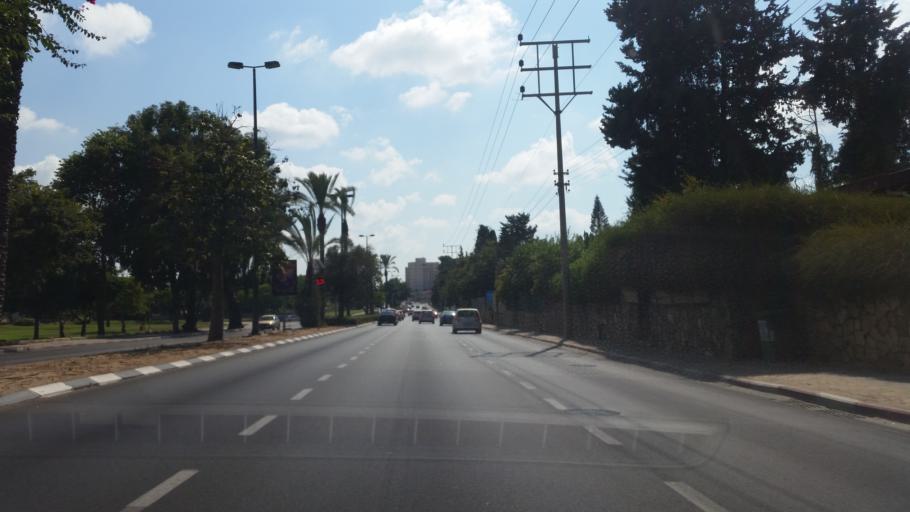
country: IL
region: Tel Aviv
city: Ramat HaSharon
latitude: 32.1275
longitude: 34.8276
